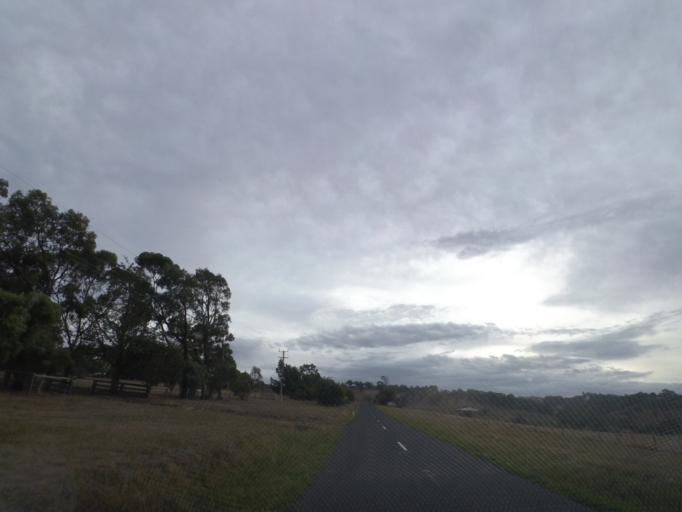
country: AU
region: Victoria
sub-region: Yarra Ranges
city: Yarra Glen
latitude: -37.6298
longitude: 145.3773
